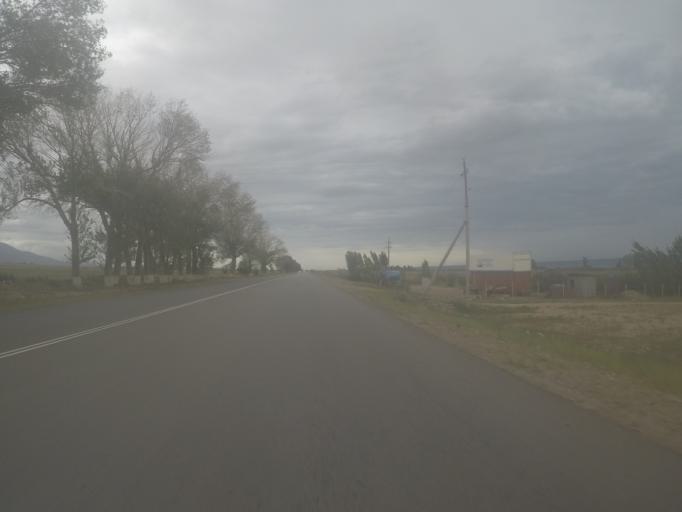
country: KG
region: Ysyk-Koel
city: Cholpon-Ata
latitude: 42.5986
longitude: 76.7950
